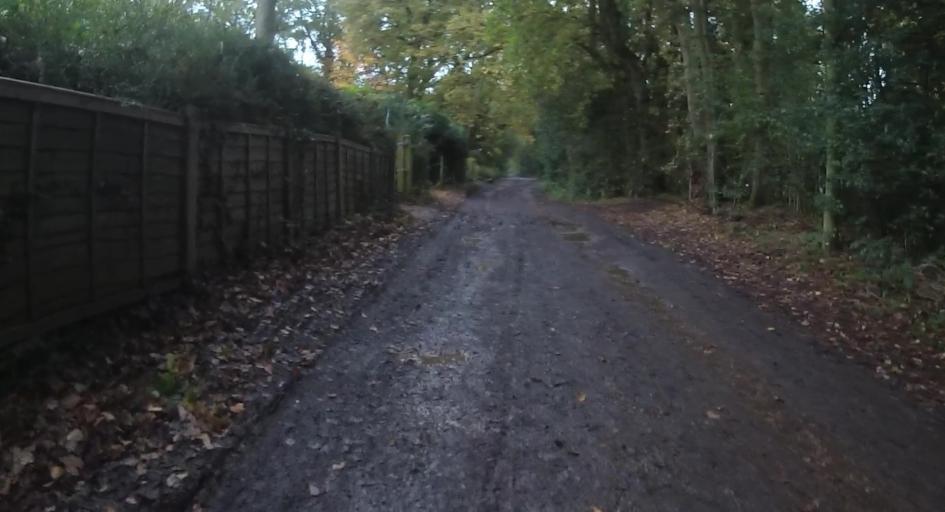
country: GB
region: England
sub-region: Surrey
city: Farnham
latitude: 51.2294
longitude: -0.8120
